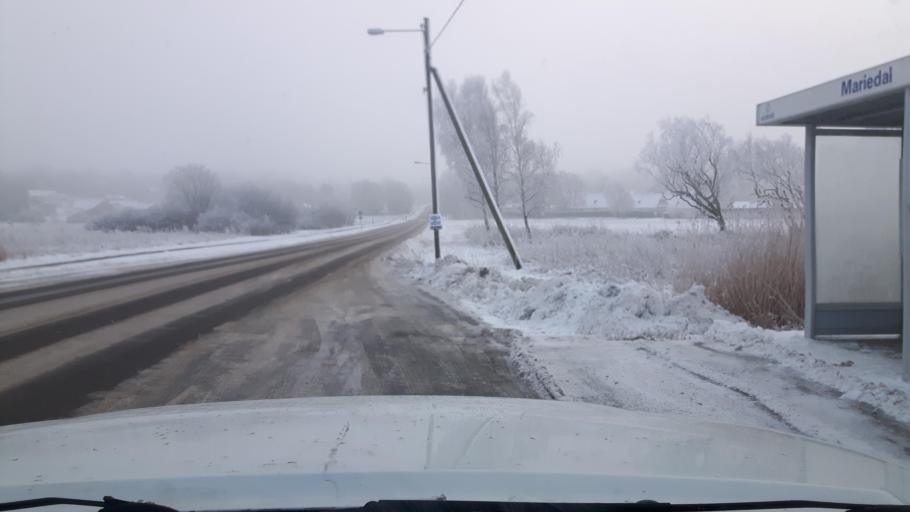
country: SE
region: Halland
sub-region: Kungsbacka Kommun
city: Onsala
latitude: 57.4050
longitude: 11.9861
